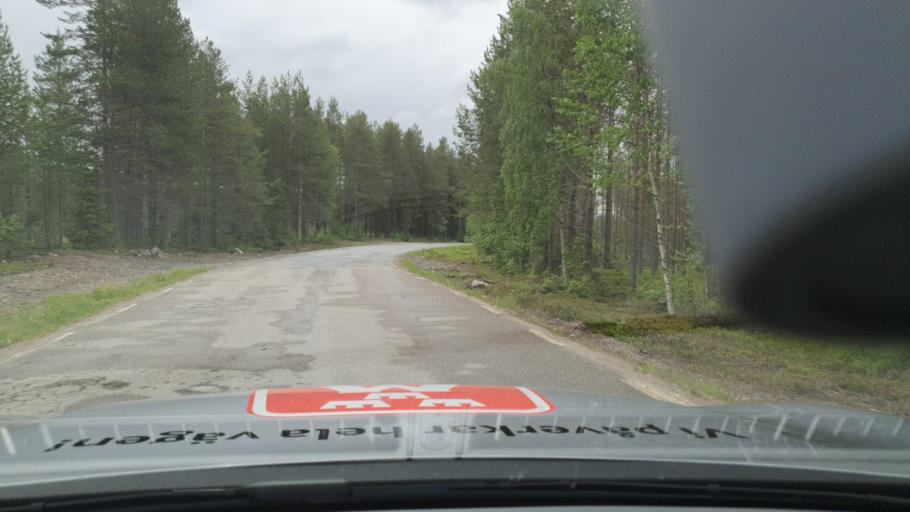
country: SE
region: Norrbotten
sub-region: Lulea Kommun
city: Ranea
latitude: 65.8031
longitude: 22.3083
